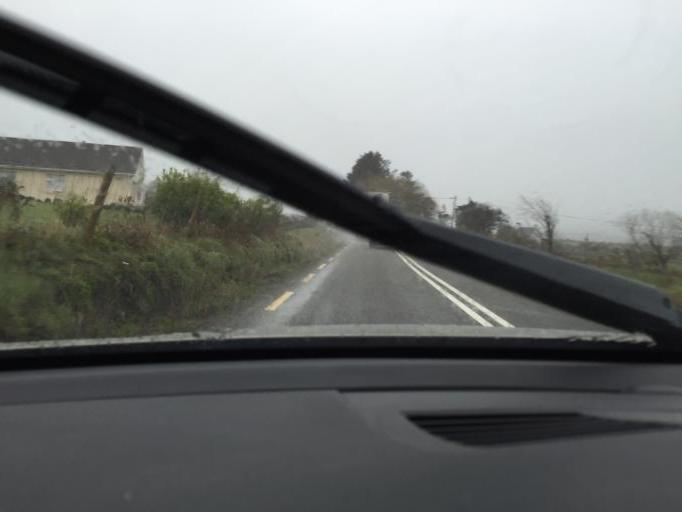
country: IE
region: Munster
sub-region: Ciarrai
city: Dingle
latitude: 52.1433
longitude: -10.1162
